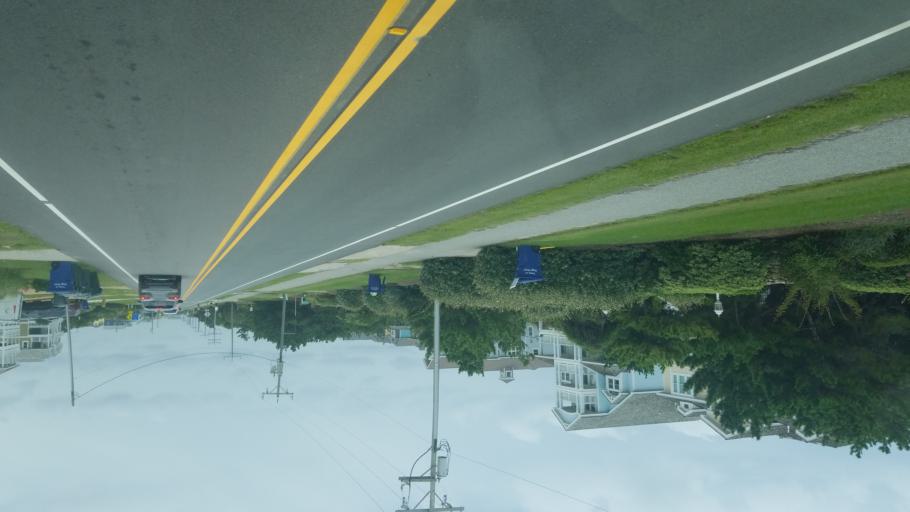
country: US
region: North Carolina
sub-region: Dare County
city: Nags Head
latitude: 35.9371
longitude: -75.6128
